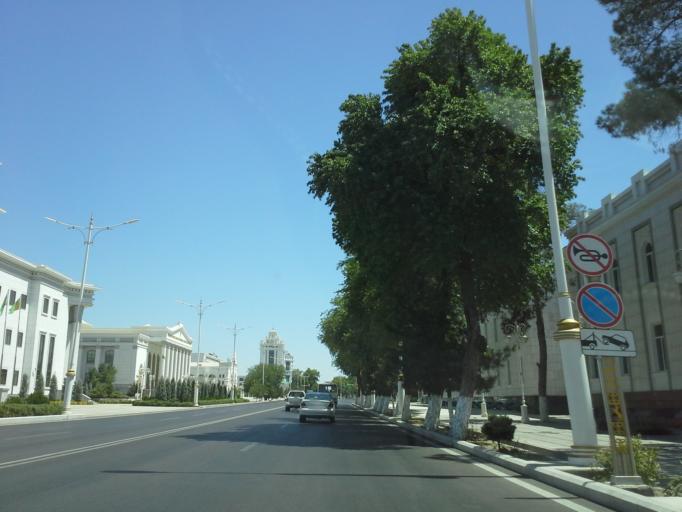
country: TM
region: Ahal
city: Ashgabat
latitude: 37.9437
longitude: 58.3850
